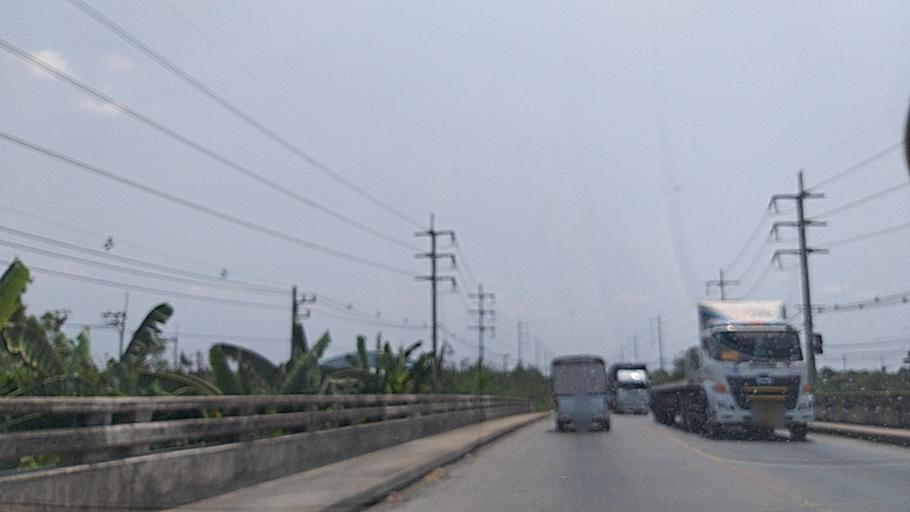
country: TH
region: Chachoengsao
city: Bang Nam Priao
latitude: 13.8437
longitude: 101.0522
